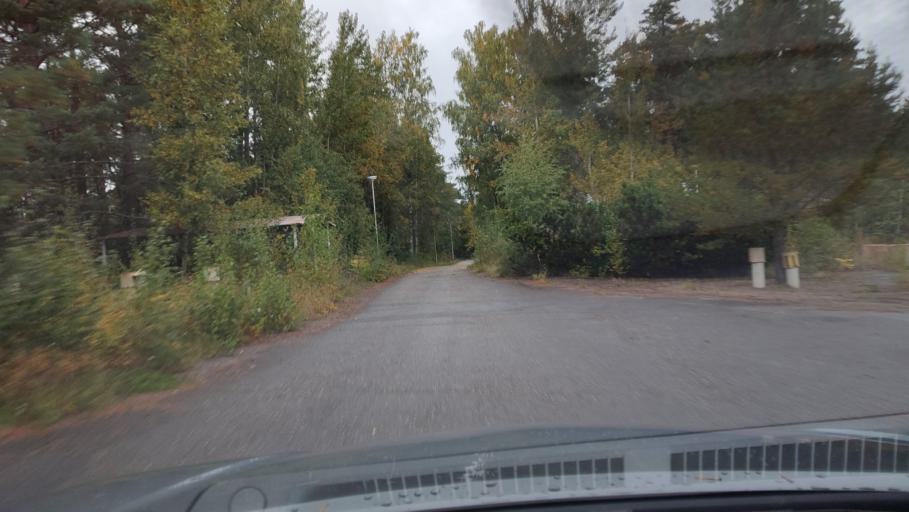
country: FI
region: Ostrobothnia
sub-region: Sydosterbotten
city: Kristinestad
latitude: 62.2738
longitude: 21.4053
